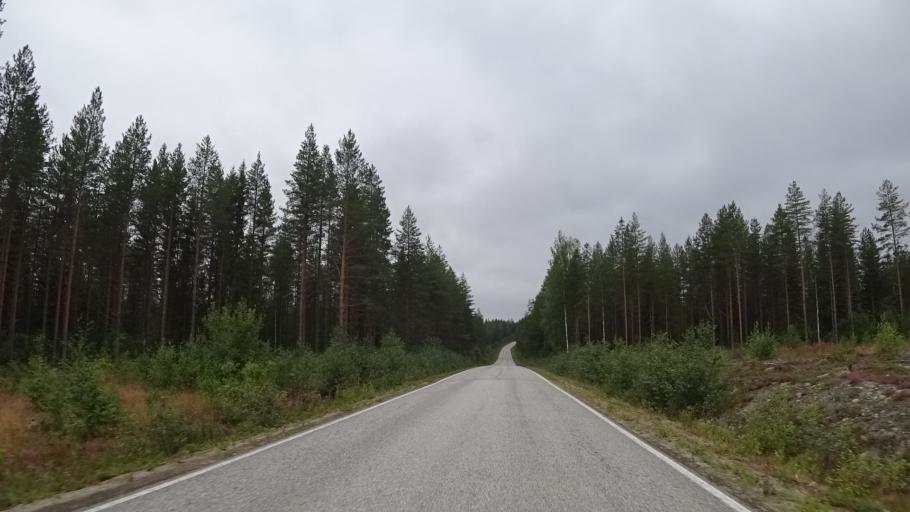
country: FI
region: North Karelia
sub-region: Pielisen Karjala
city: Lieksa
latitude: 63.3670
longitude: 30.2905
